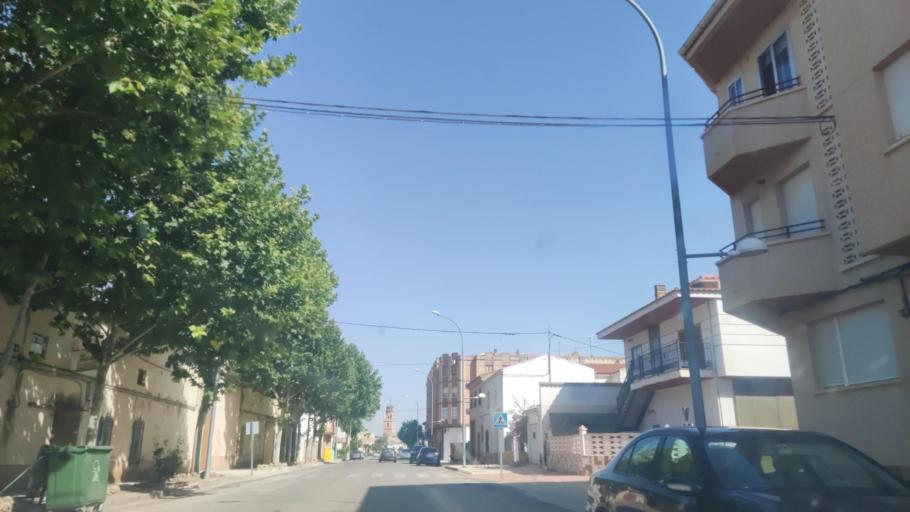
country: ES
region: Castille-La Mancha
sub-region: Provincia de Albacete
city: La Gineta
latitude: 39.1105
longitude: -1.9936
